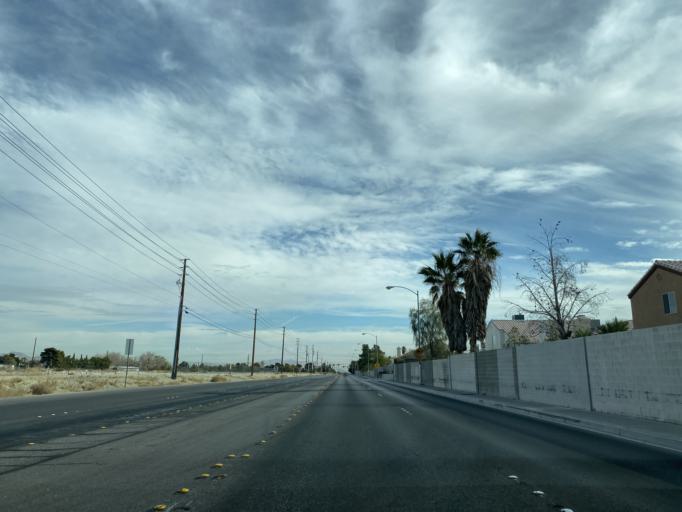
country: US
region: Nevada
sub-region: Clark County
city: North Las Vegas
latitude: 36.2468
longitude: -115.1940
